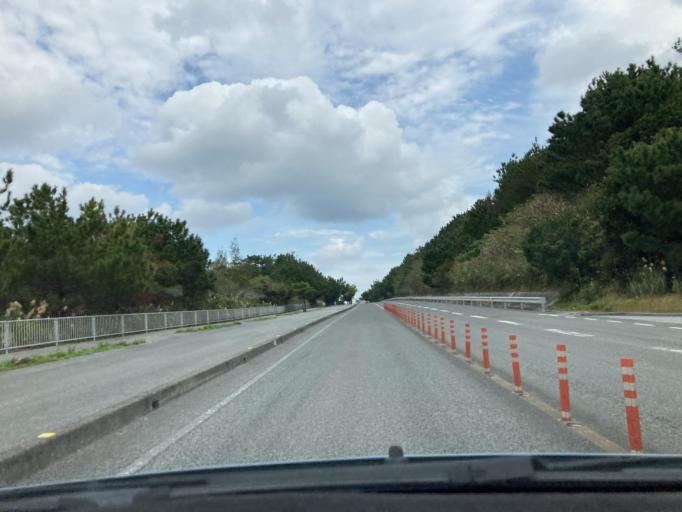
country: JP
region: Okinawa
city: Ishikawa
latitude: 26.4587
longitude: 127.8240
